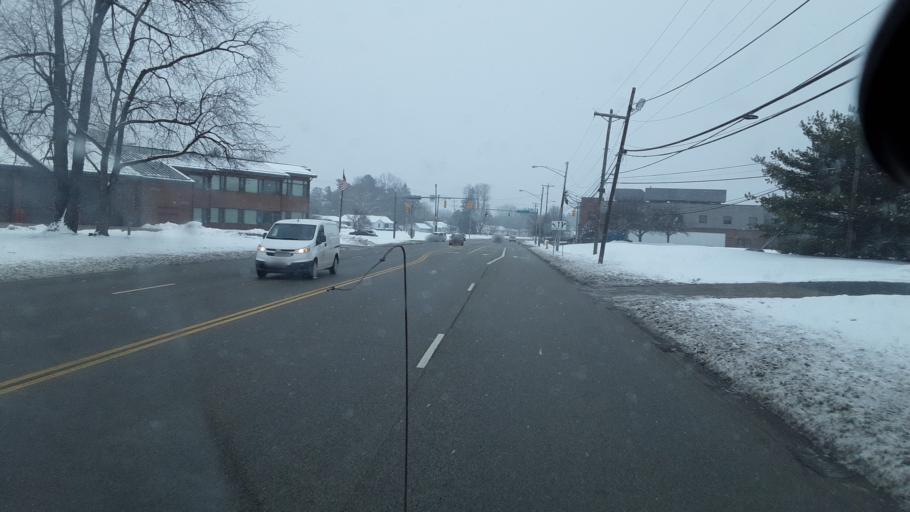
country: US
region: Ohio
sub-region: Licking County
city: Heath
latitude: 40.0420
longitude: -82.4670
